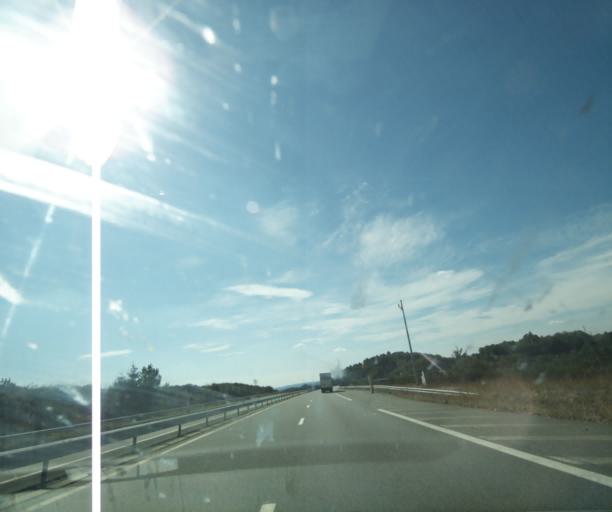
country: FR
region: Limousin
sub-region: Departement de la Correze
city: Naves
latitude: 45.3078
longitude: 1.8329
